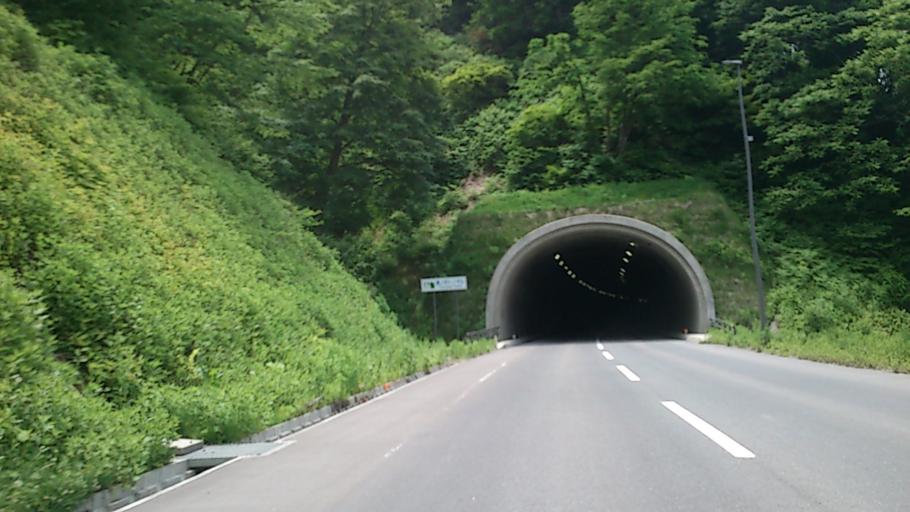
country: JP
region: Aomori
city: Hirosaki
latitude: 40.5338
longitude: 140.2539
